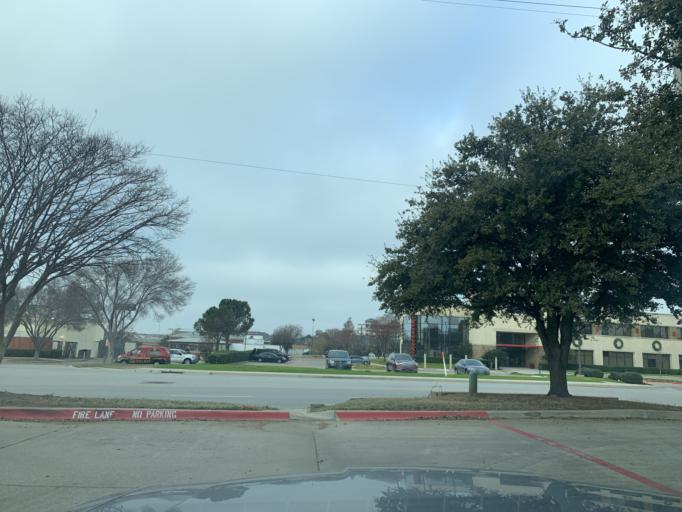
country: US
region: Texas
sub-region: Tarrant County
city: Bedford
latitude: 32.8381
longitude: -97.1417
